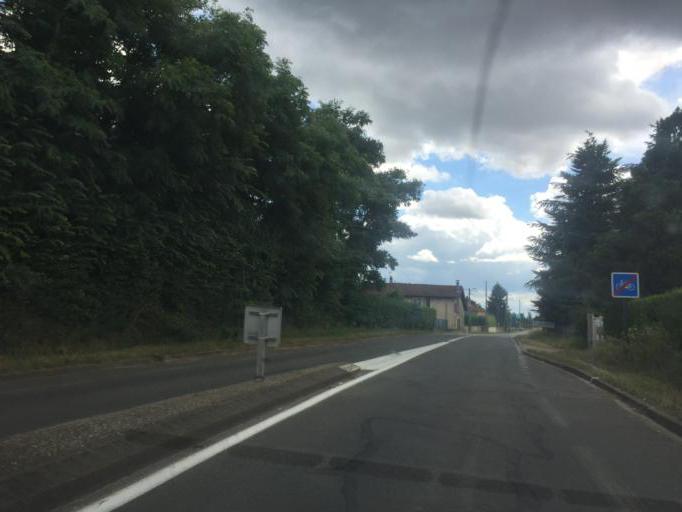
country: FR
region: Rhone-Alpes
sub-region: Departement de l'Isere
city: Pont-de-Cheruy
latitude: 45.7630
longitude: 5.1918
